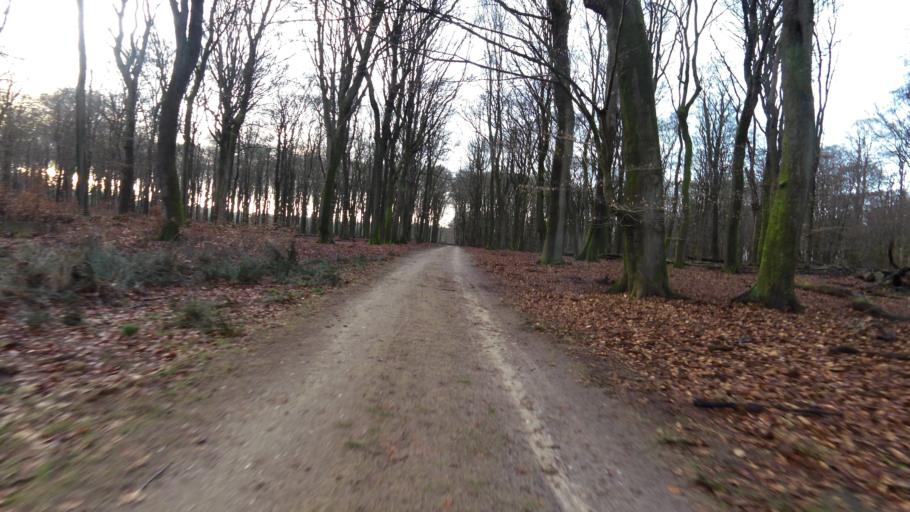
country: NL
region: Gelderland
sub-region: Gemeente Epe
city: Vaassen
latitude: 52.3151
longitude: 5.8734
